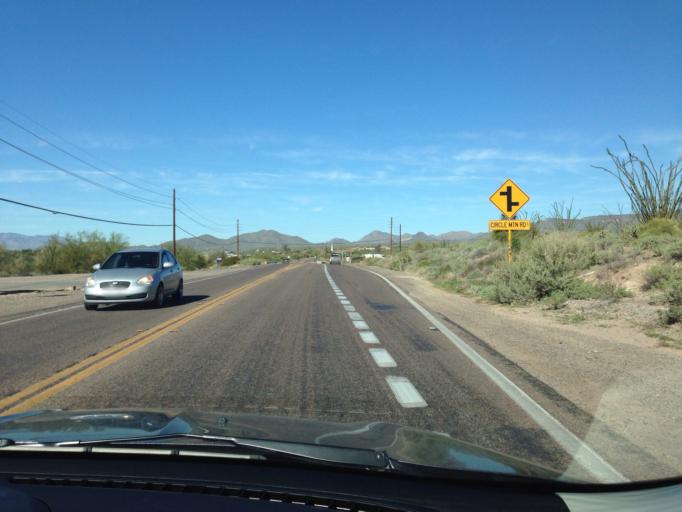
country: US
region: Arizona
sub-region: Maricopa County
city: New River
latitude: 33.8831
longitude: -112.0722
